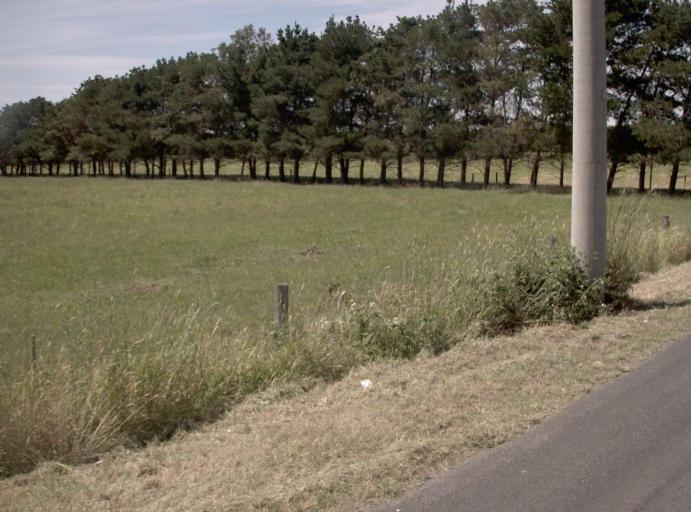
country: AU
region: Victoria
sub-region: Latrobe
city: Traralgon
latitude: -38.1735
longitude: 146.6611
